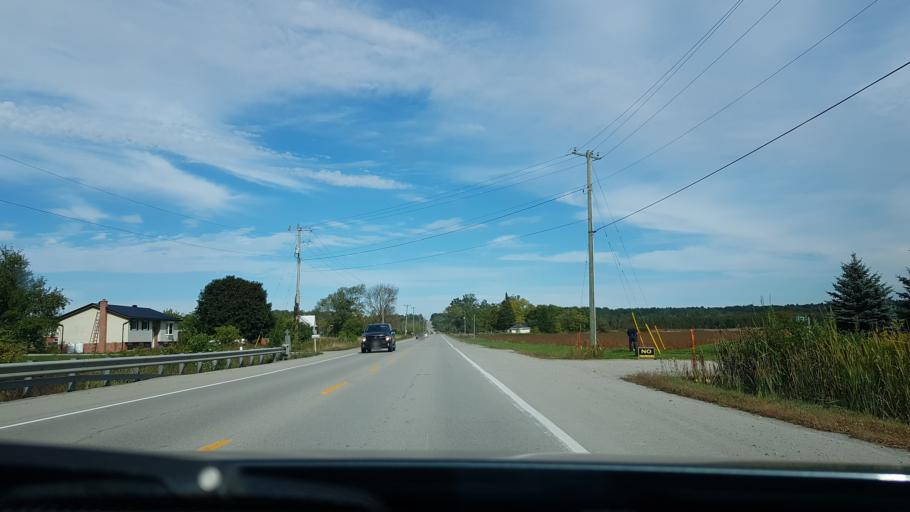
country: CA
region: Ontario
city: Angus
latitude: 44.4758
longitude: -79.8441
